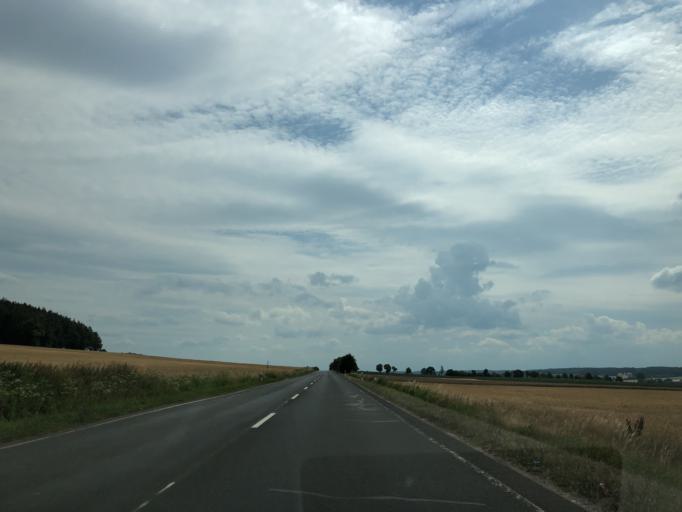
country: DE
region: Bavaria
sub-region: Regierungsbezirk Mittelfranken
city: Wachenroth
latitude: 49.7518
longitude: 10.7320
